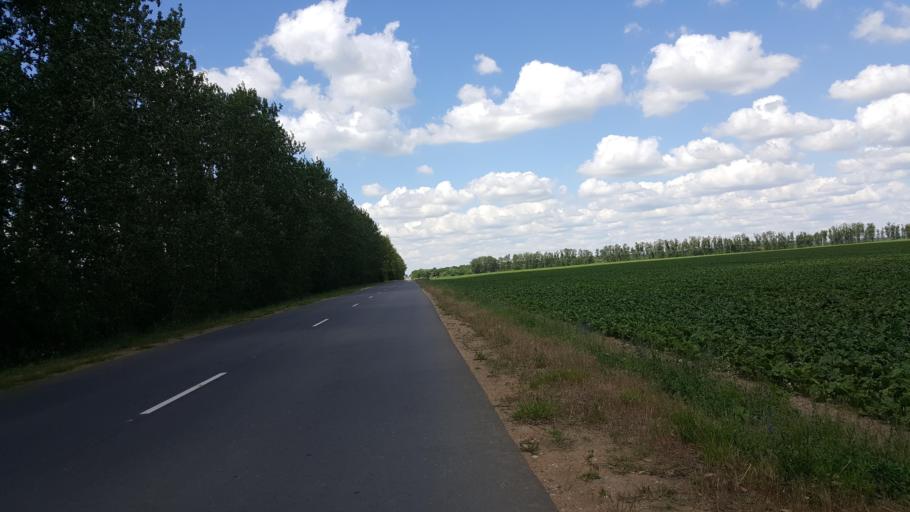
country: BY
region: Brest
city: Vysokaye
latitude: 52.3726
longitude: 23.5825
